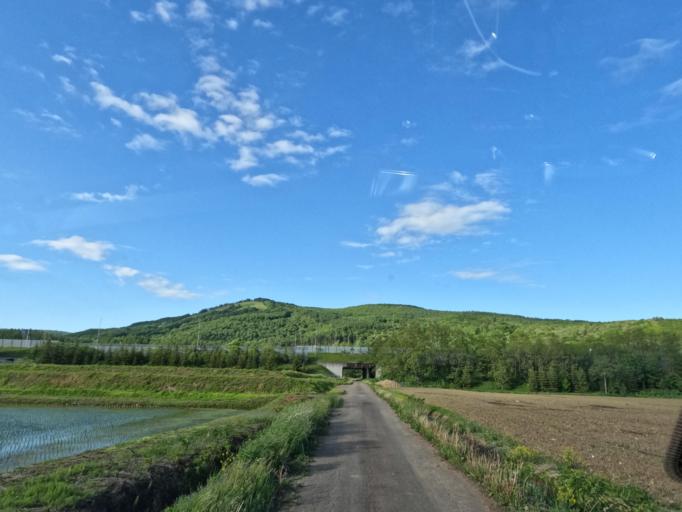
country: JP
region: Hokkaido
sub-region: Asahikawa-shi
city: Asahikawa
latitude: 43.9200
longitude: 142.4941
